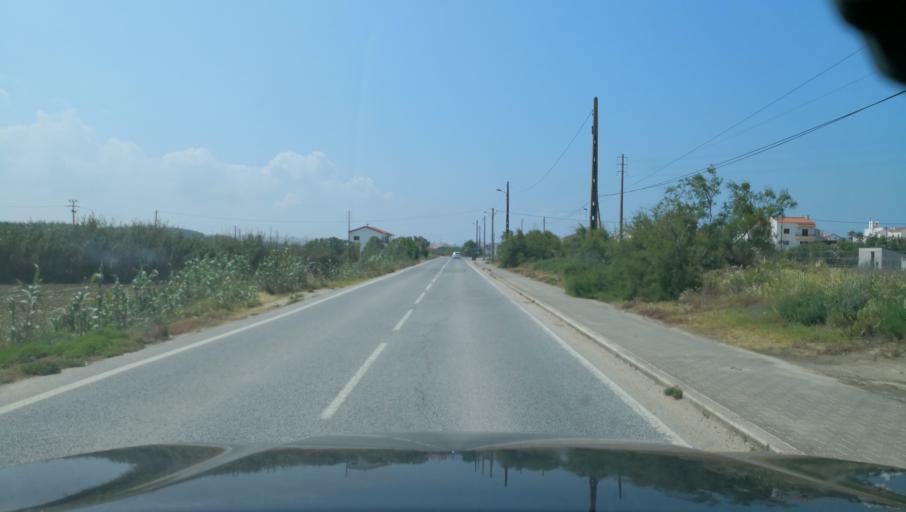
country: PT
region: Leiria
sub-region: Peniche
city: Atouguia da Baleia
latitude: 39.3418
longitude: -9.3524
